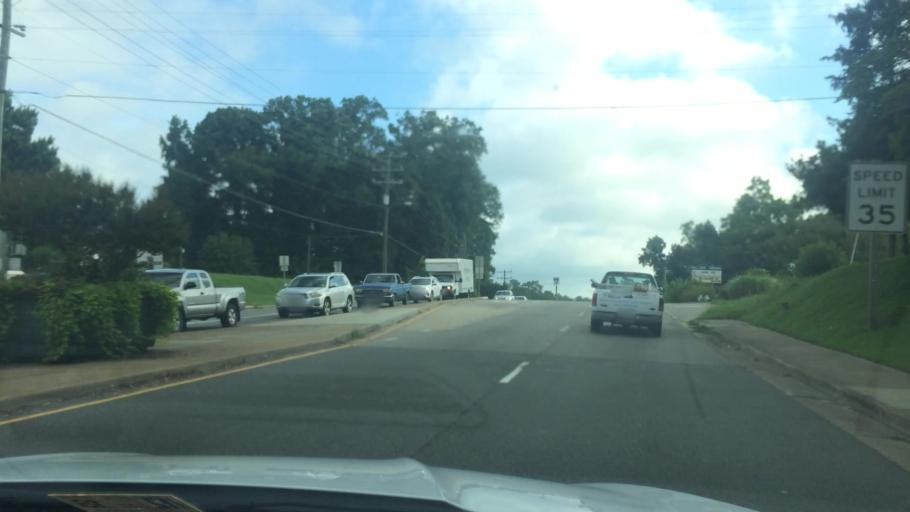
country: US
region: Virginia
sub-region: Gloucester County
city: Gloucester Courthouse
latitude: 37.4124
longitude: -76.5200
